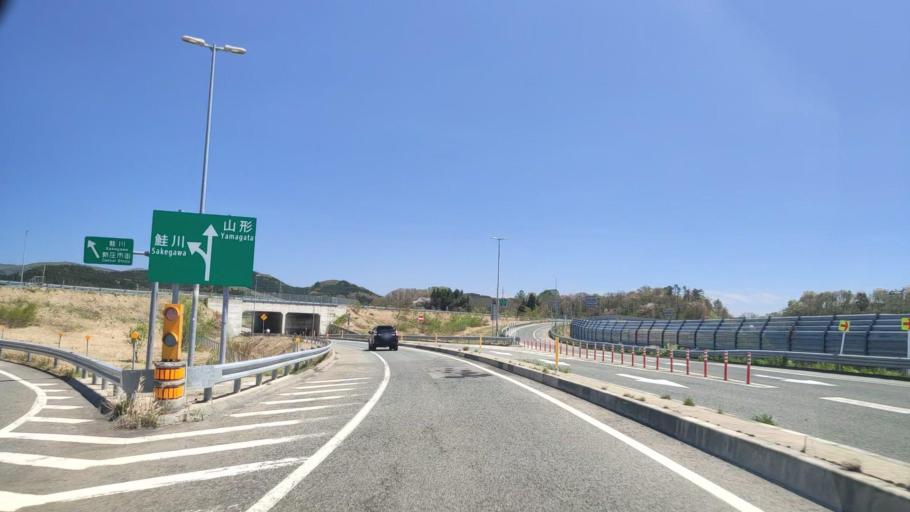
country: JP
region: Yamagata
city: Shinjo
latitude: 38.7396
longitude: 140.2966
